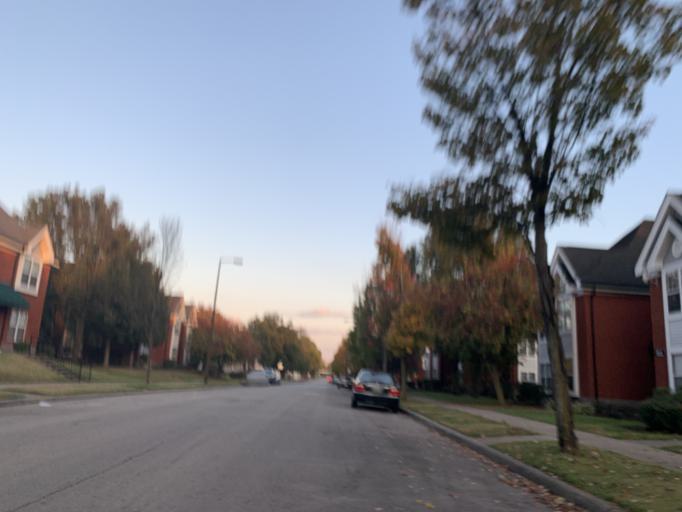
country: US
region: Kentucky
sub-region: Jefferson County
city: Louisville
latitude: 38.2523
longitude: -85.7786
